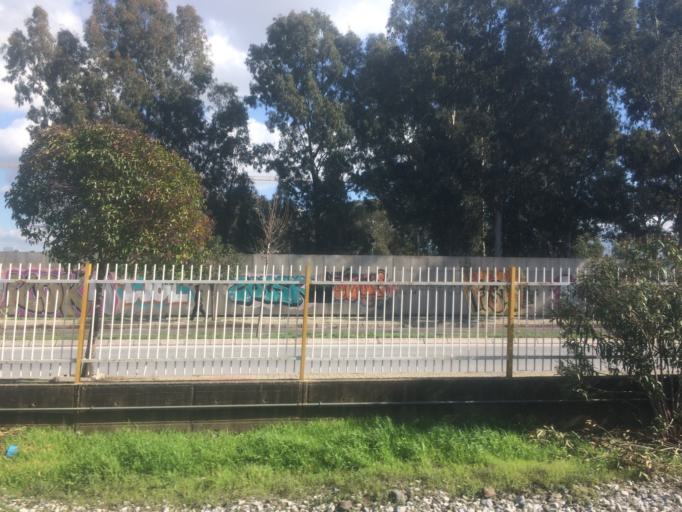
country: TR
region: Izmir
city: Buca
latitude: 38.4430
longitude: 27.1737
